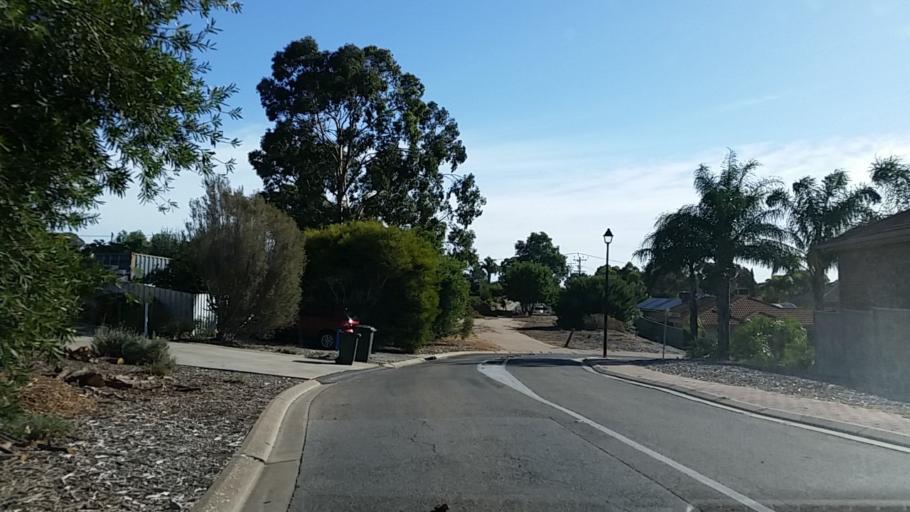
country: AU
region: South Australia
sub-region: Campbelltown
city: Athelstone
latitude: -34.8619
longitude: 138.7115
